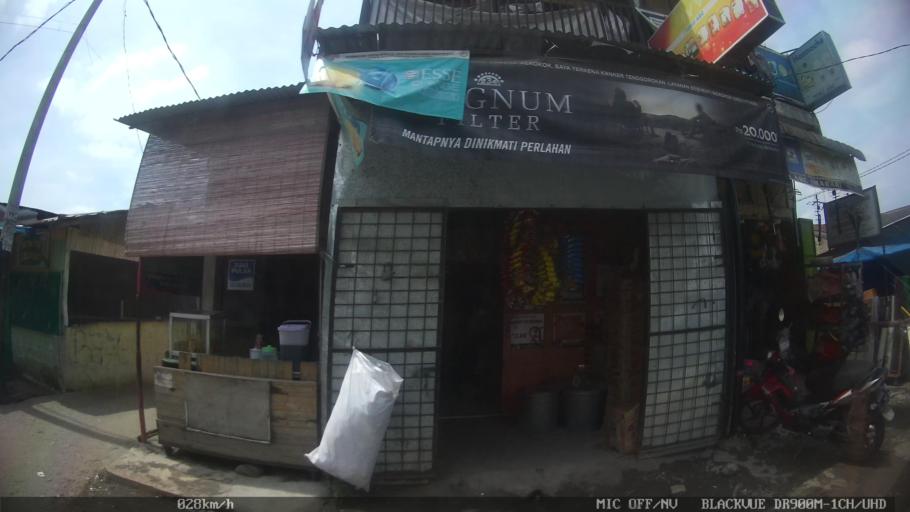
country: ID
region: North Sumatra
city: Medan
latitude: 3.6511
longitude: 98.6923
